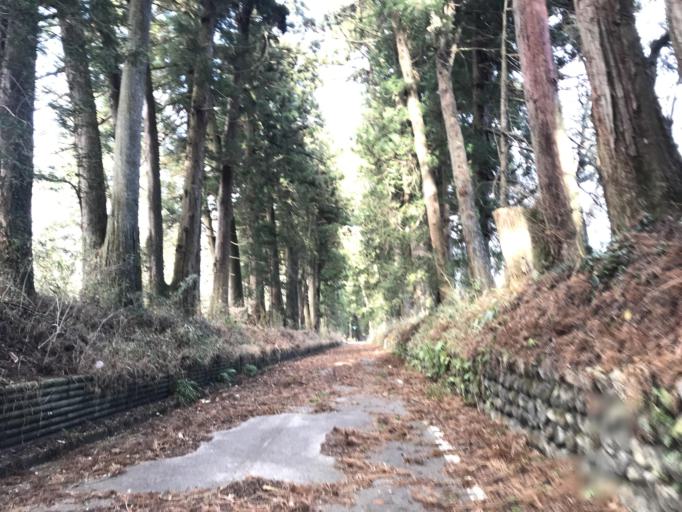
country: JP
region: Tochigi
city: Imaichi
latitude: 36.6828
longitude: 139.7190
